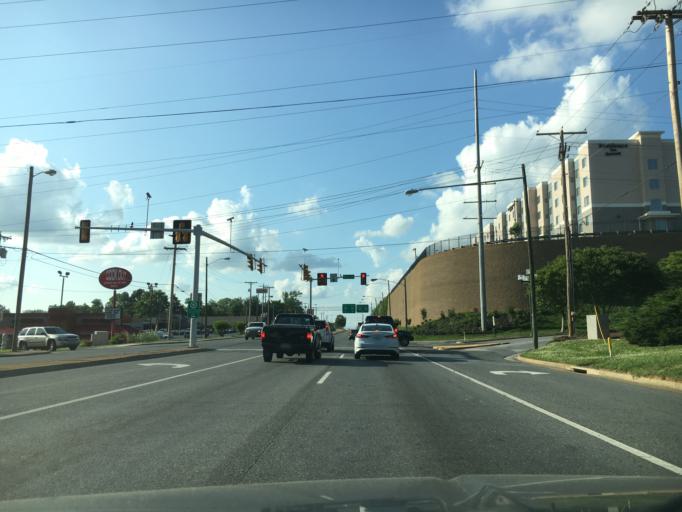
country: US
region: Virginia
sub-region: City of Lynchburg
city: West Lynchburg
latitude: 37.3612
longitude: -79.1811
